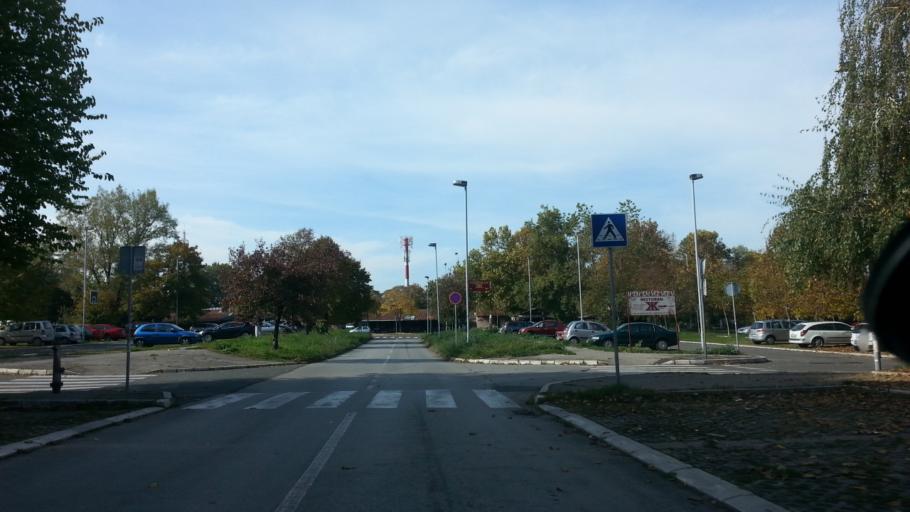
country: RS
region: Central Serbia
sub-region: Belgrade
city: Zemun
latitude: 44.8166
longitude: 20.3723
